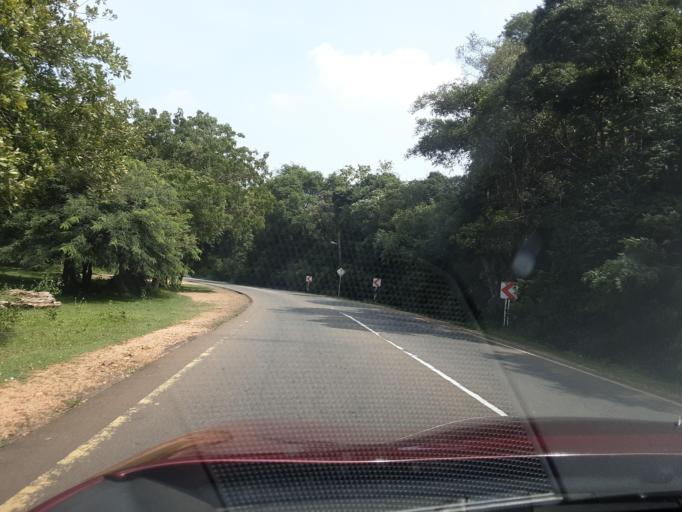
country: LK
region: North Central
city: Anuradhapura
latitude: 8.3480
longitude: 80.5076
